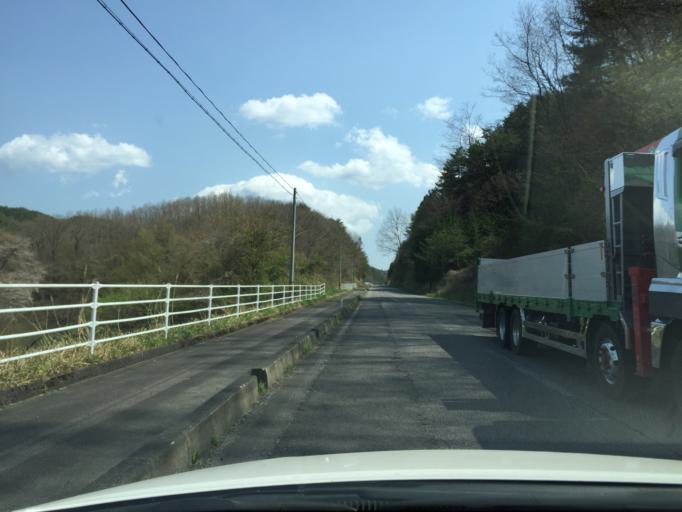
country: JP
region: Fukushima
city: Namie
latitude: 37.4077
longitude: 140.7962
